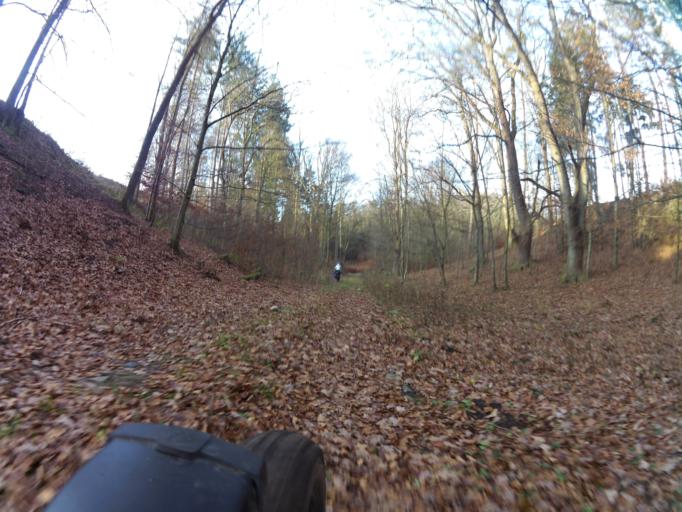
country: PL
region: West Pomeranian Voivodeship
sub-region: Powiat koszalinski
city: Polanow
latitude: 54.0799
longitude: 16.6596
